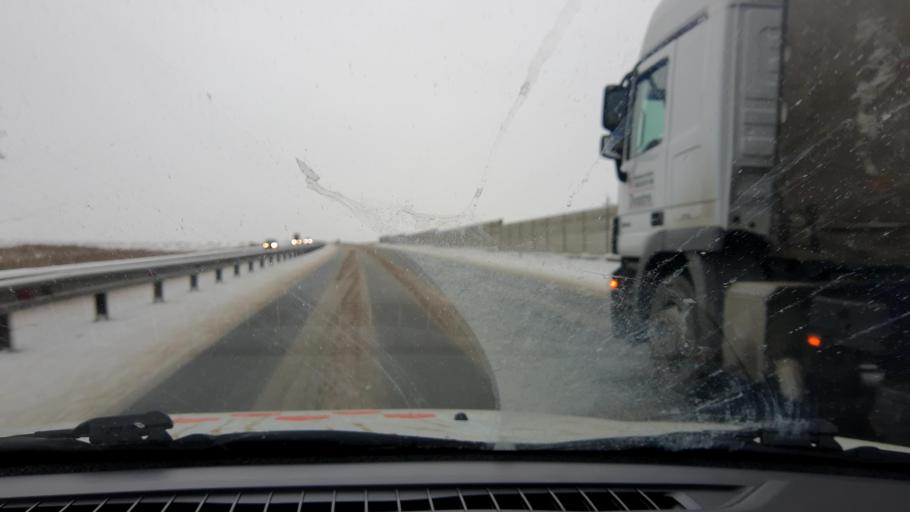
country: RU
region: Nizjnij Novgorod
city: Burevestnik
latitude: 56.1156
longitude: 43.9581
